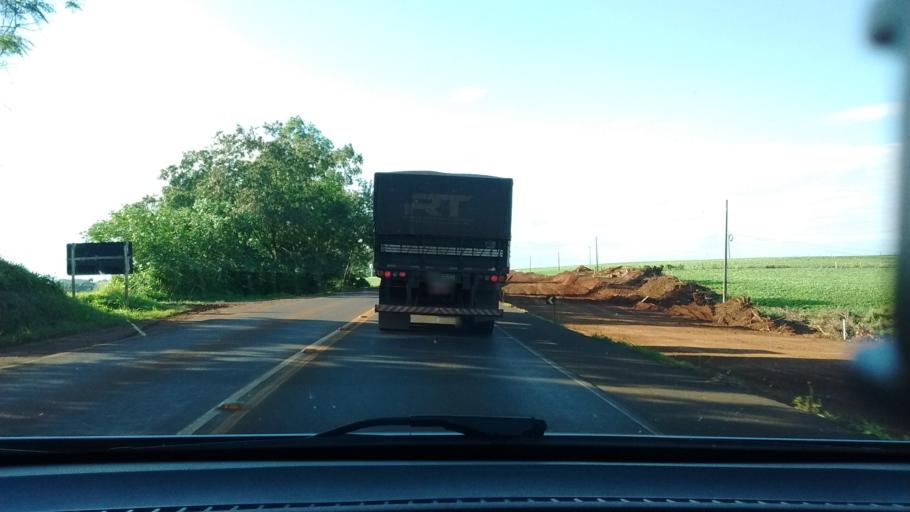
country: BR
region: Parana
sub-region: Cascavel
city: Cascavel
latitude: -25.2171
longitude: -53.5954
